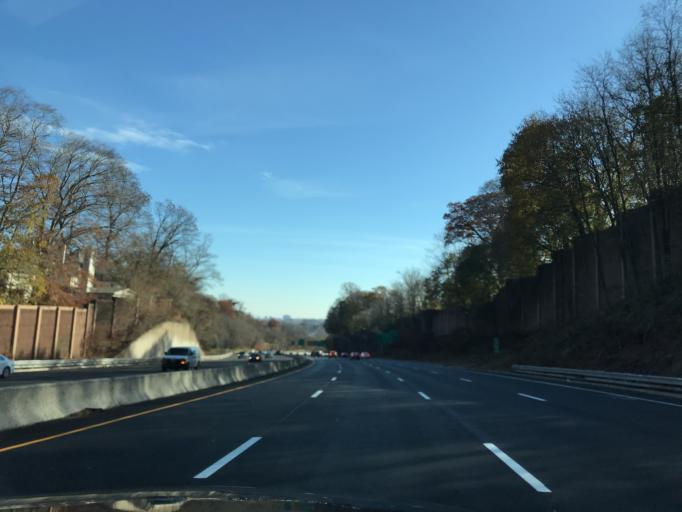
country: US
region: New Jersey
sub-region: Essex County
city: West Orange
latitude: 40.7847
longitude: -74.2473
